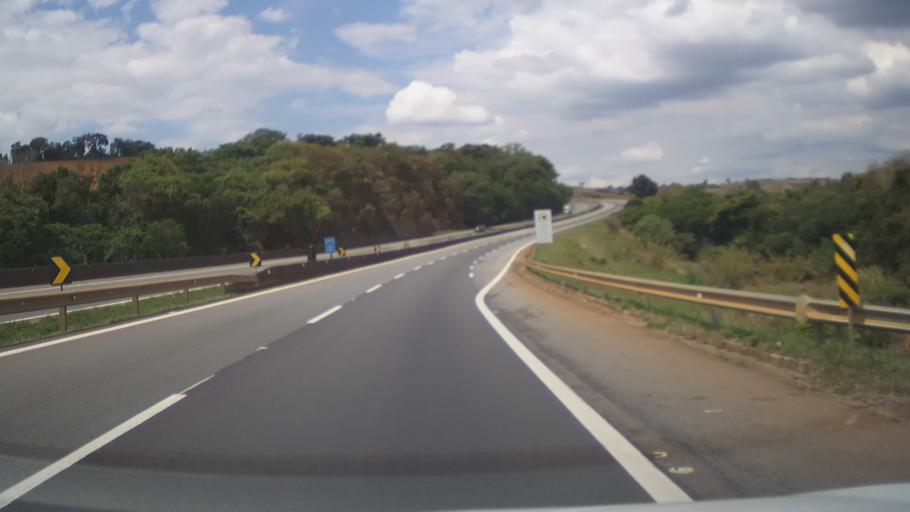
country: BR
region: Minas Gerais
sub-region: Nepomuceno
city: Nepomuceno
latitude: -21.2881
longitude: -45.1456
